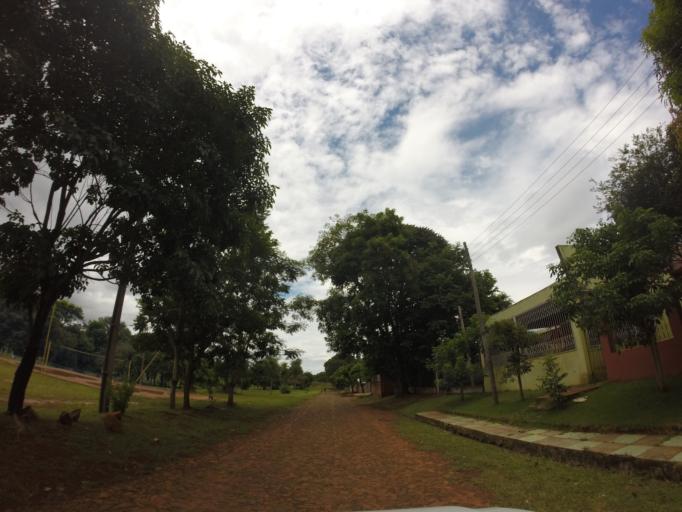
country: PY
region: Alto Parana
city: Ciudad del Este
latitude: -25.4124
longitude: -54.6289
